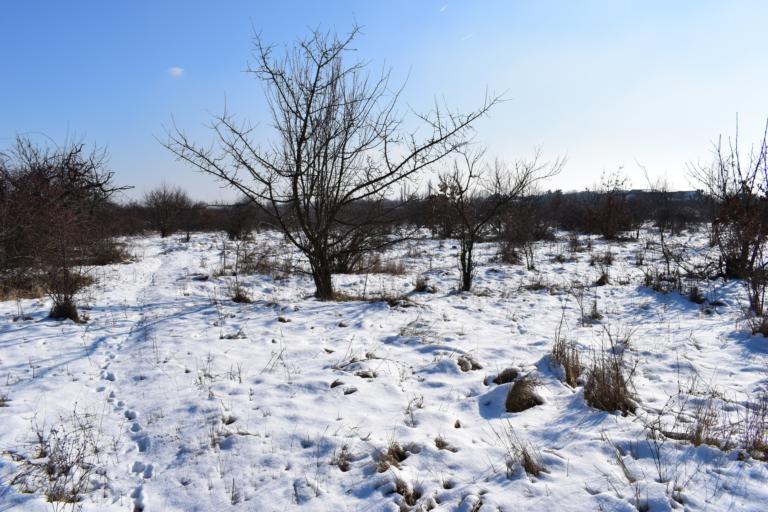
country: RO
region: Ilfov
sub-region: Comuna Otopeni
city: Otopeni
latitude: 44.5053
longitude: 26.0678
